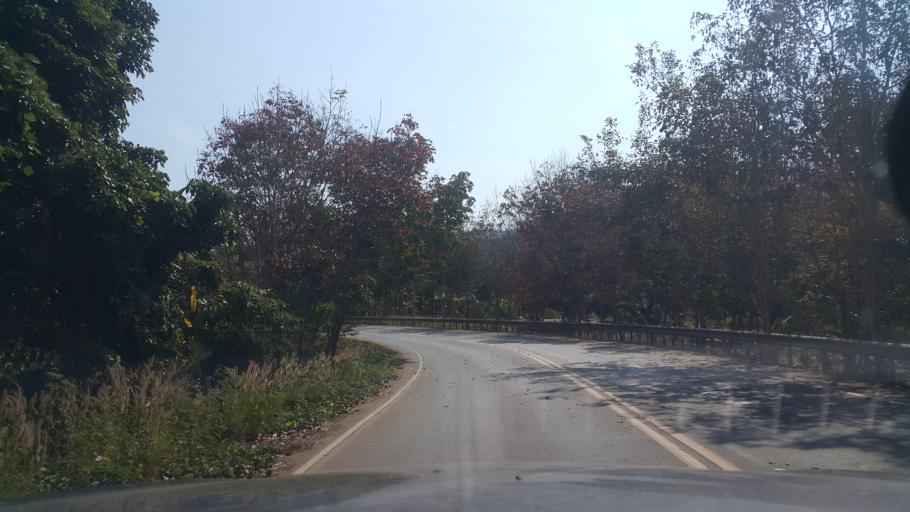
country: TH
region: Loei
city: Pak Chom
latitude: 18.1024
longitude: 102.0159
